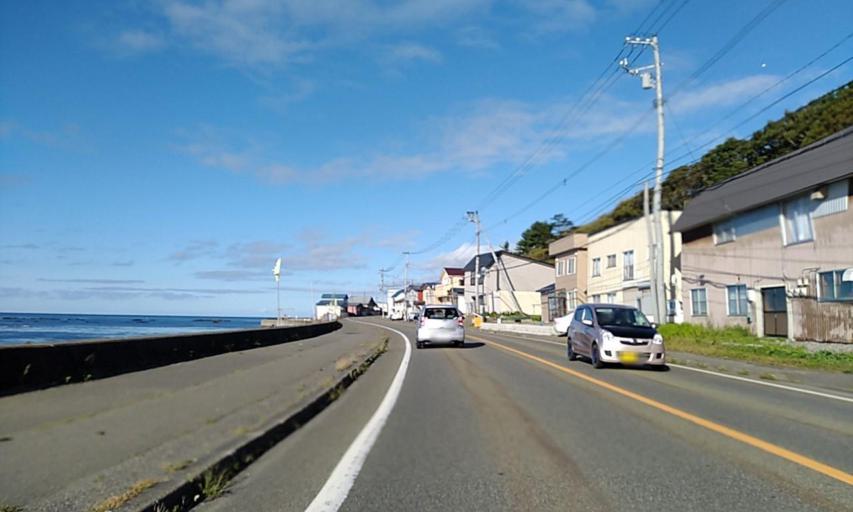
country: JP
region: Hokkaido
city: Shizunai-furukawacho
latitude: 42.1771
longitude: 142.7406
